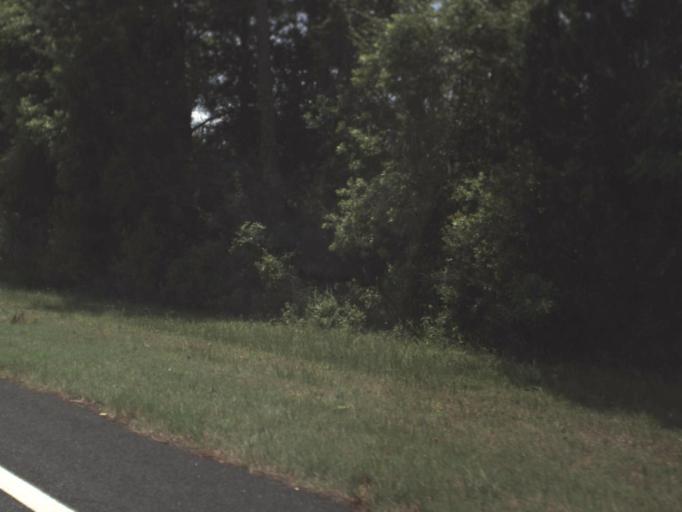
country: US
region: Florida
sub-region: Taylor County
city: Steinhatchee
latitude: 29.7179
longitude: -83.3047
